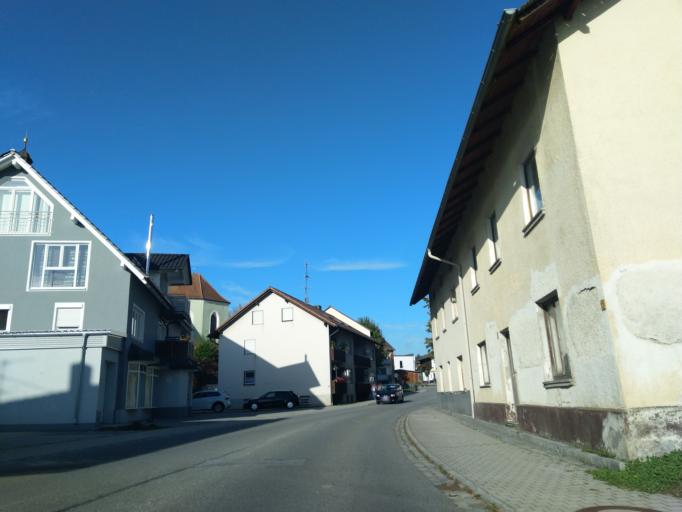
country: DE
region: Bavaria
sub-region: Lower Bavaria
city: Metten
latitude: 48.8607
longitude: 12.8926
